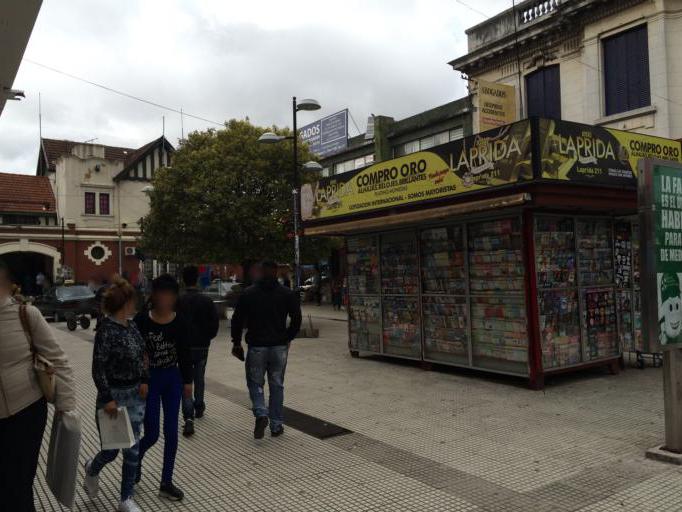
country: AR
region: Buenos Aires
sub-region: Partido de Lomas de Zamora
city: Lomas de Zamora
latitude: -34.7608
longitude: -58.3983
